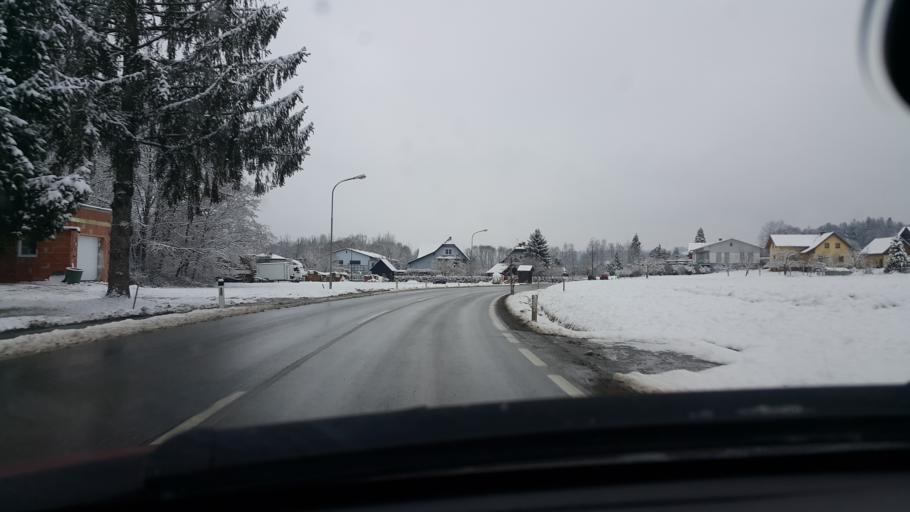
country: AT
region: Styria
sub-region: Politischer Bezirk Graz-Umgebung
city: Hitzendorf
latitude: 47.0422
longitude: 15.2931
